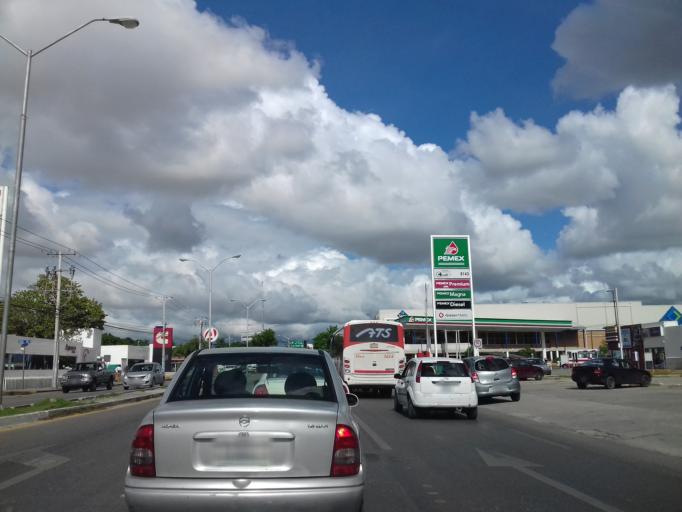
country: MX
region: Yucatan
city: Merida
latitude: 20.9483
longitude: -89.6506
